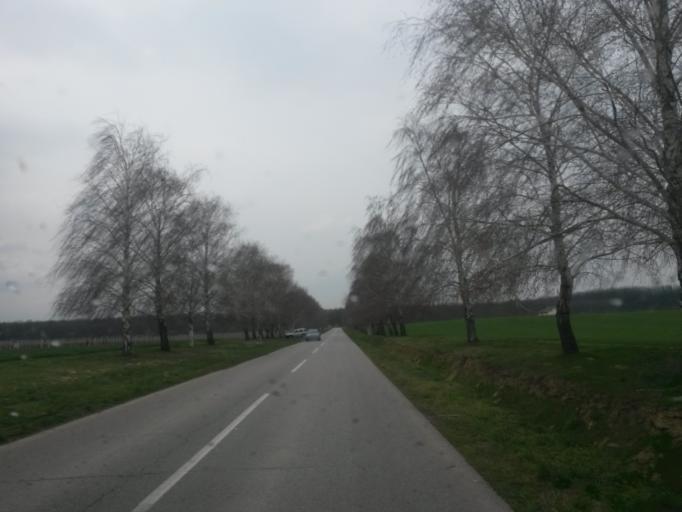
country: HR
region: Vukovarsko-Srijemska
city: Lovas
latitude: 45.2162
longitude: 19.1499
